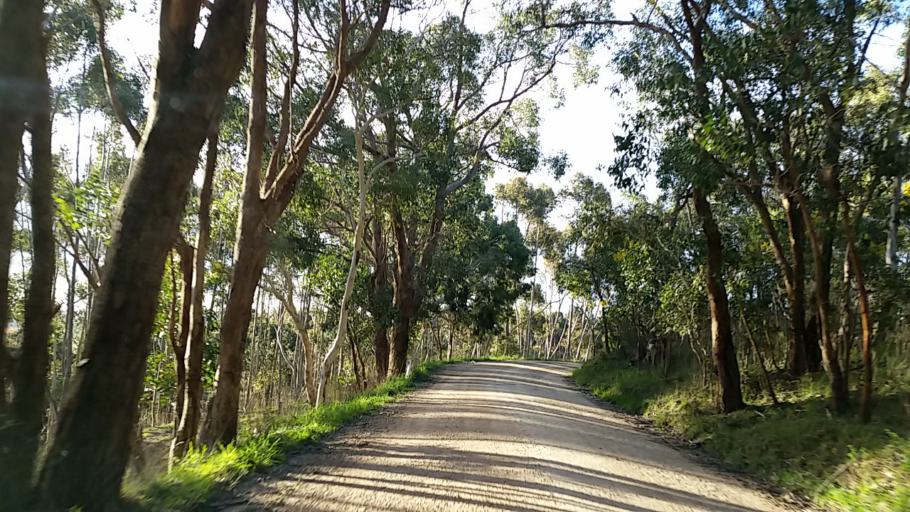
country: AU
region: South Australia
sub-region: Adelaide Hills
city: Lobethal
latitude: -34.9015
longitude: 138.8081
